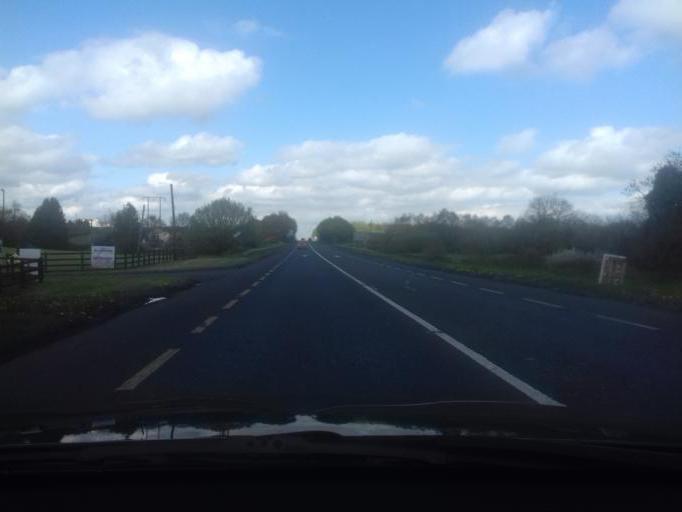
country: IE
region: Leinster
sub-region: Laois
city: Portlaoise
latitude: 53.0475
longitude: -7.2456
